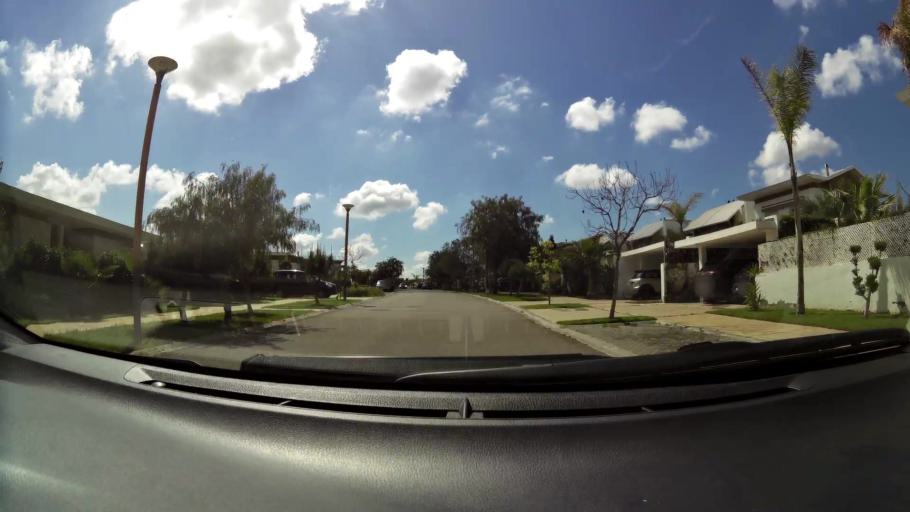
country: MA
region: Grand Casablanca
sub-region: Nouaceur
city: Bouskoura
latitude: 33.4925
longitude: -7.5931
